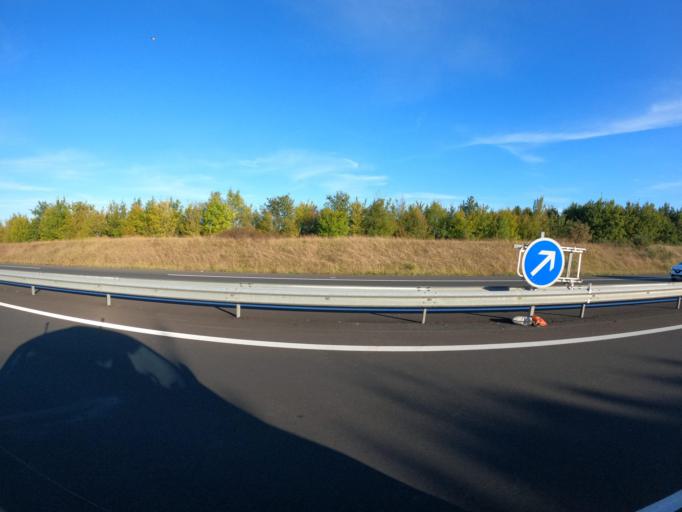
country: FR
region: Pays de la Loire
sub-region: Departement de la Vendee
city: Mortagne-sur-Sevre
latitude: 46.9939
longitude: -0.9128
